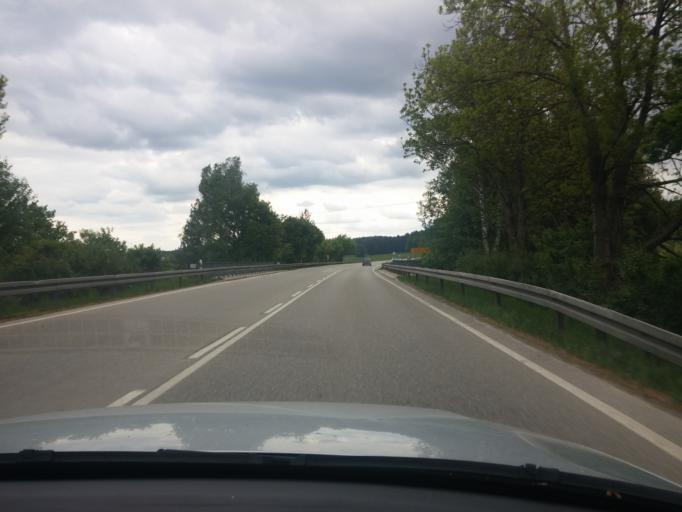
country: DE
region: Bavaria
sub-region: Upper Bavaria
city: Sachsenkam
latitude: 47.8112
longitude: 11.6514
